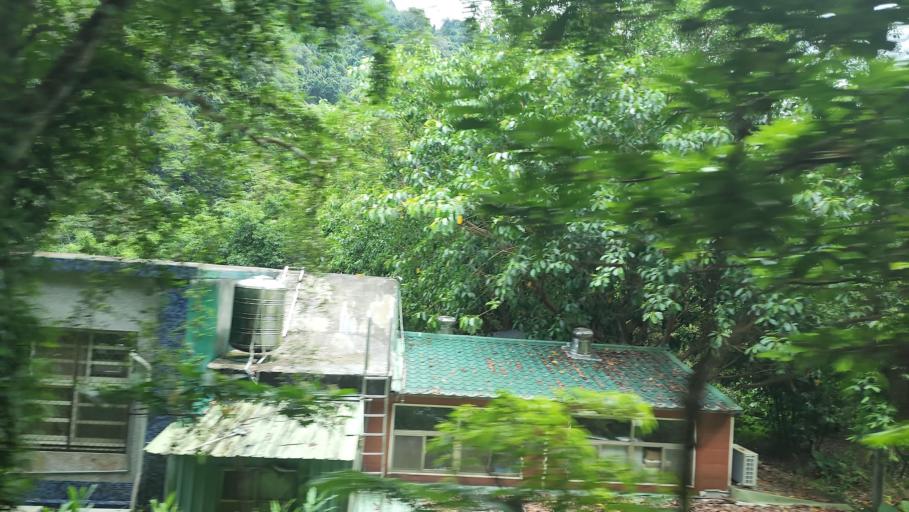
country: TW
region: Taiwan
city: Daxi
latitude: 24.8741
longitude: 121.3846
